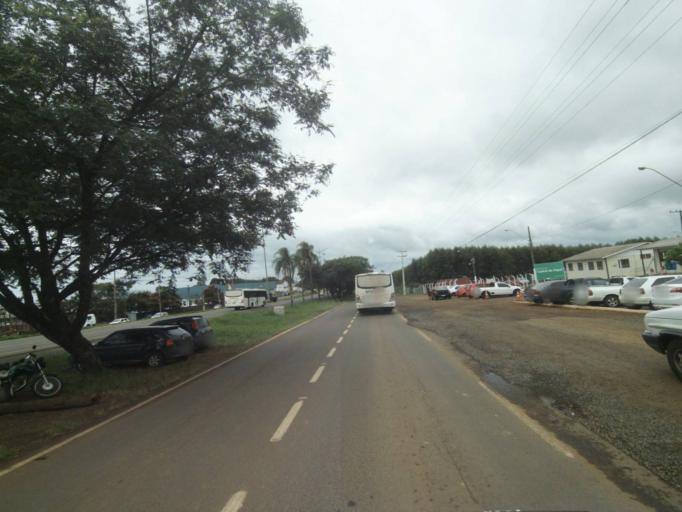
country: BR
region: Parana
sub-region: Telemaco Borba
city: Telemaco Borba
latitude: -24.3389
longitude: -50.6563
